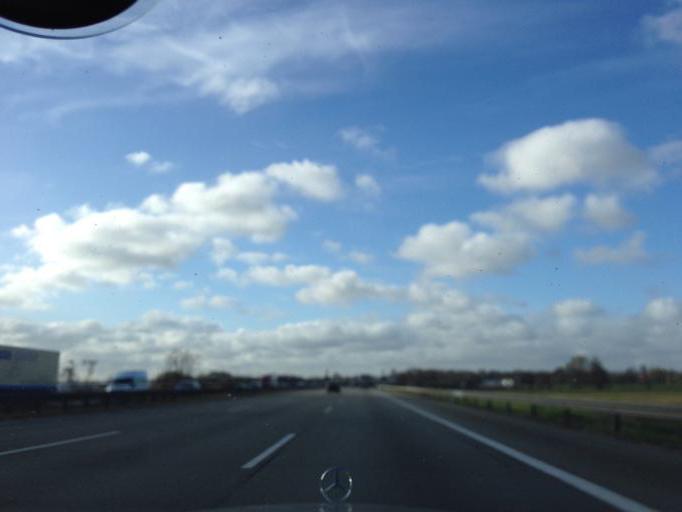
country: DE
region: Hamburg
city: Harburg
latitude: 53.4324
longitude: 10.0332
